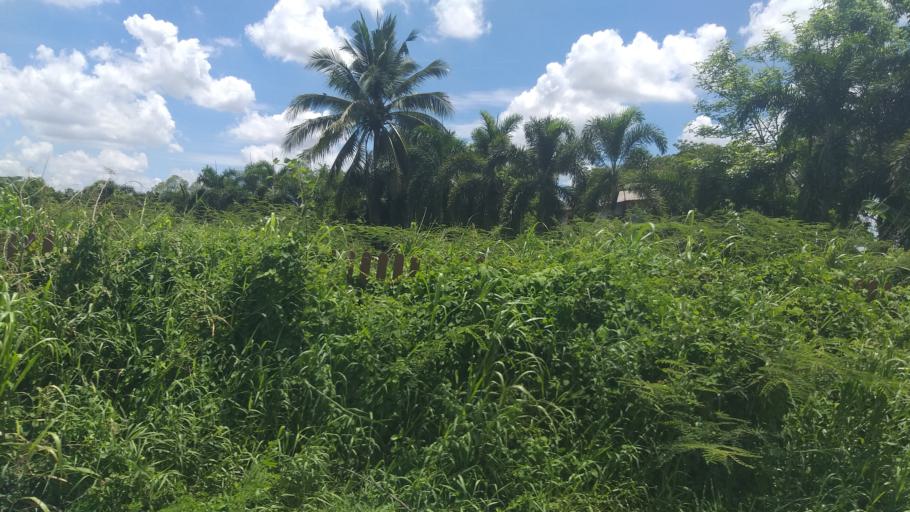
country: TH
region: Nakhon Nayok
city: Ban Na
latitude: 14.2836
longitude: 101.0669
